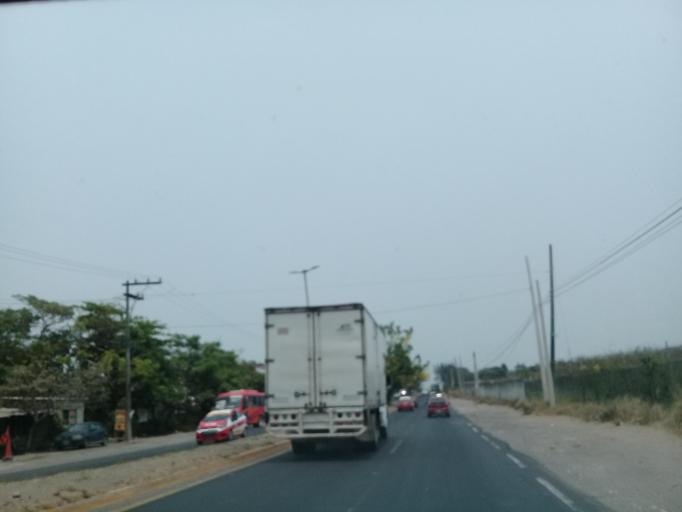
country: MX
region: Veracruz
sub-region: Veracruz
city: Las Amapolas
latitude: 19.1549
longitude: -96.1874
